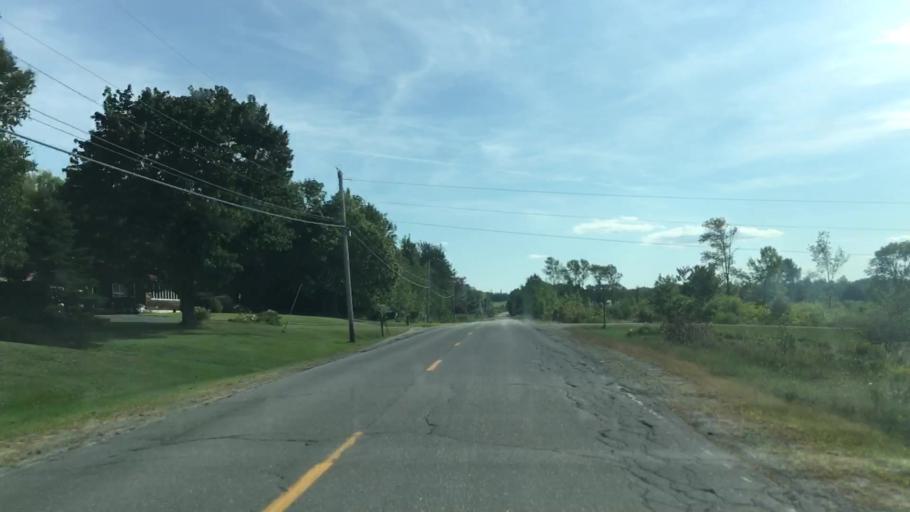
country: US
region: Maine
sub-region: Penobscot County
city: Lincoln
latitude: 45.3282
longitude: -68.5314
